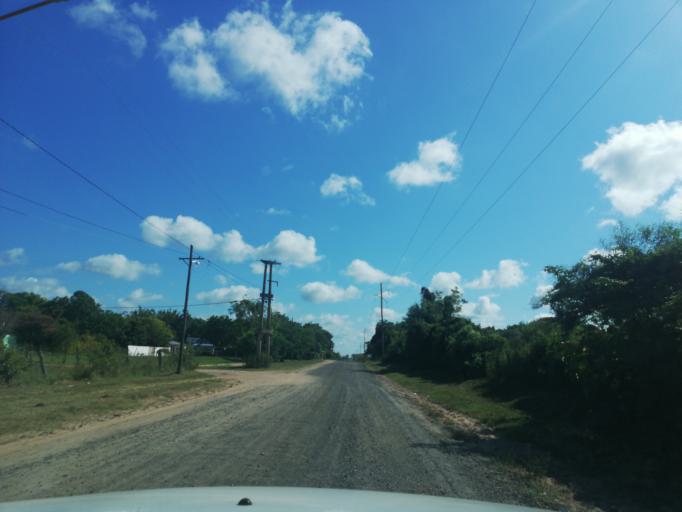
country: AR
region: Corrientes
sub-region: Departamento de San Miguel
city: San Miguel
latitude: -27.9879
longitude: -57.5859
